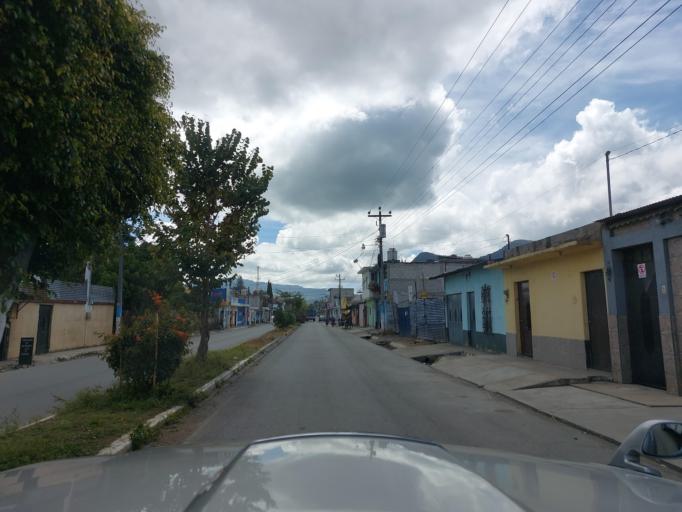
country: GT
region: Chimaltenango
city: Parramos
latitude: 14.6092
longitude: -90.8056
